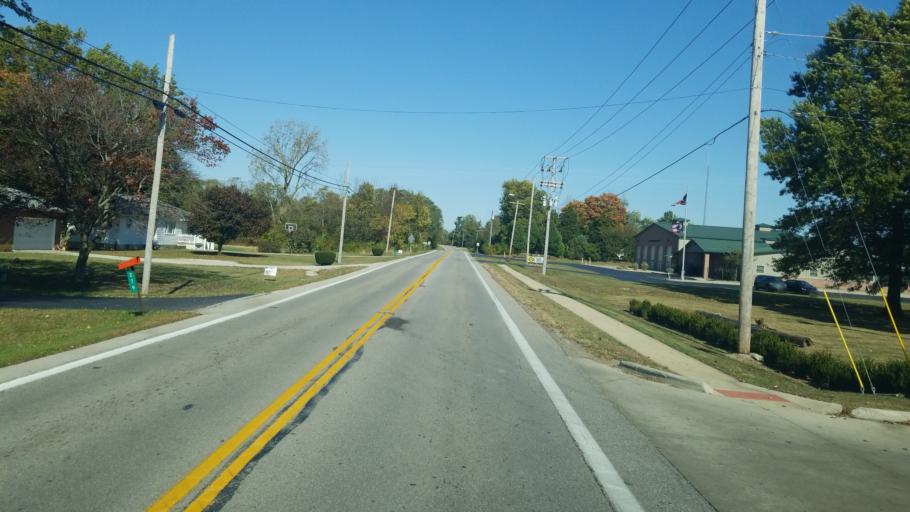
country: US
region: Ohio
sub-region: Marion County
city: Prospect
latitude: 40.4627
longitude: -83.0784
